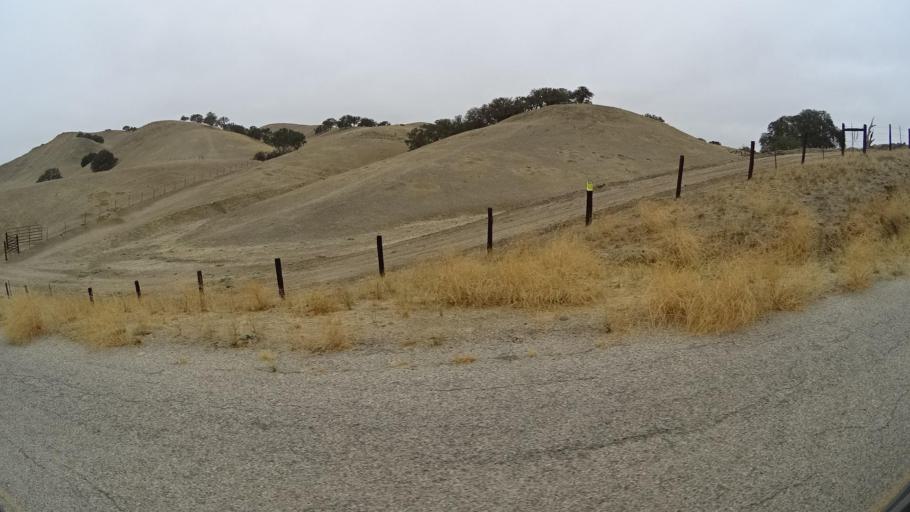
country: US
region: California
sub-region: San Luis Obispo County
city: San Miguel
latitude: 35.8632
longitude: -120.7658
